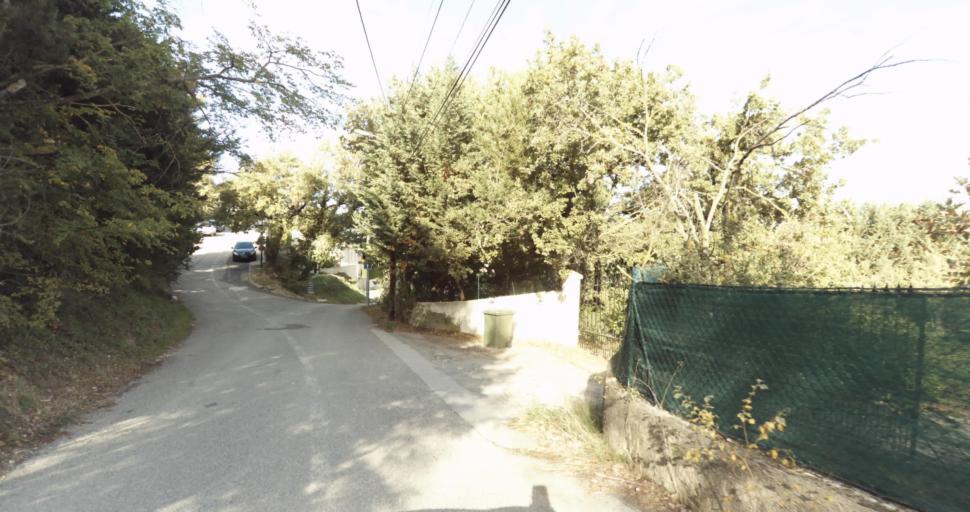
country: FR
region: Provence-Alpes-Cote d'Azur
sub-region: Departement des Bouches-du-Rhone
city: Venelles
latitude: 43.6028
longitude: 5.4852
